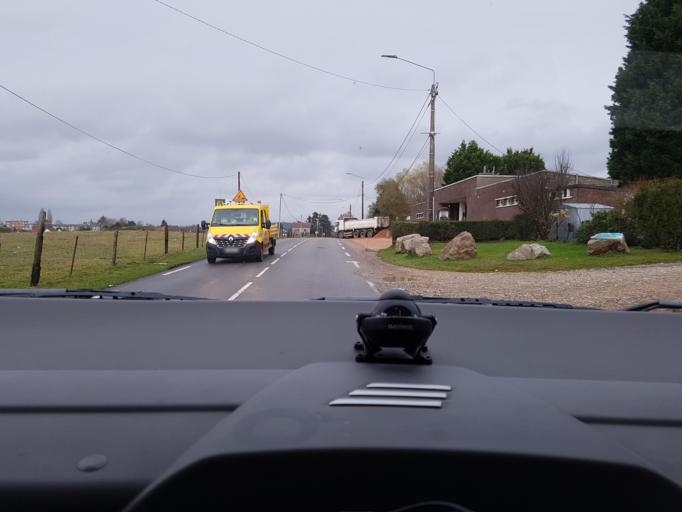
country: FR
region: Haute-Normandie
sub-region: Departement de la Seine-Maritime
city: Gournay-en-Bray
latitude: 49.4735
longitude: 1.7128
